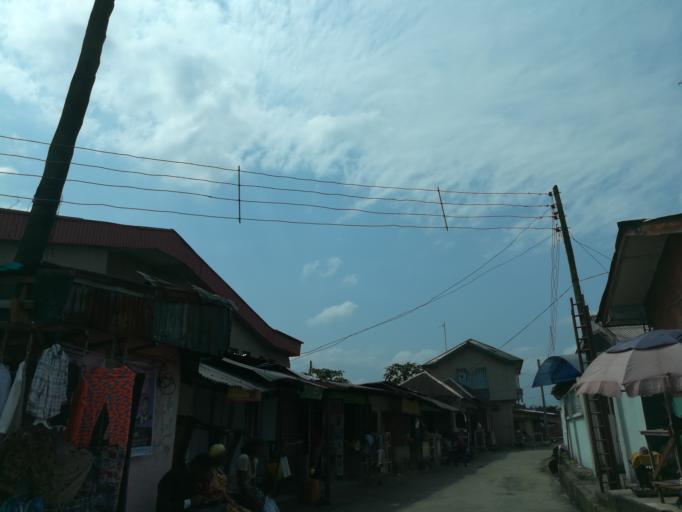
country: NG
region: Rivers
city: Port Harcourt
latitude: 4.8276
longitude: 6.9808
